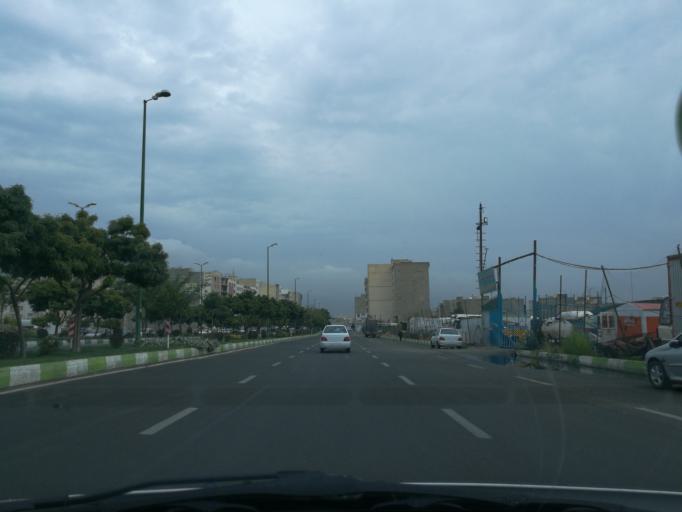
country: IR
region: Alborz
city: Karaj
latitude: 35.8536
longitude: 50.9598
